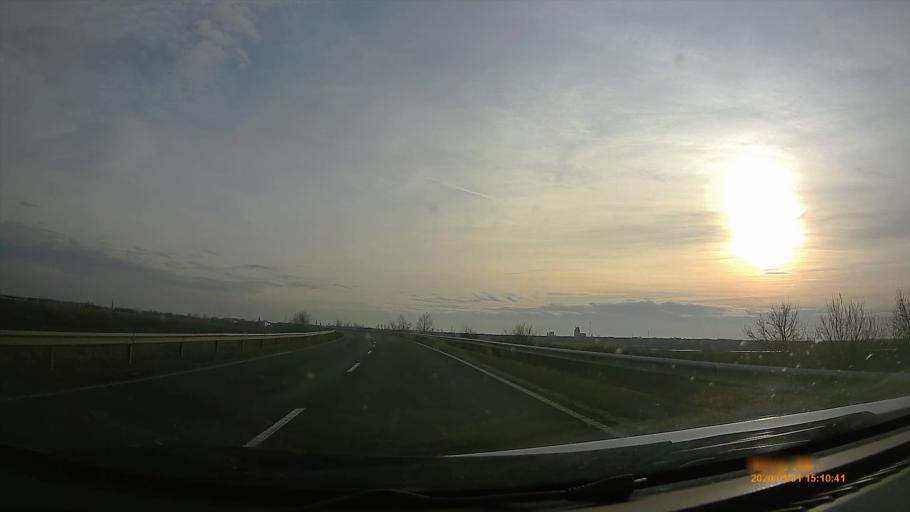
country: HU
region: Hajdu-Bihar
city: Polgar
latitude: 47.8586
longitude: 21.1507
